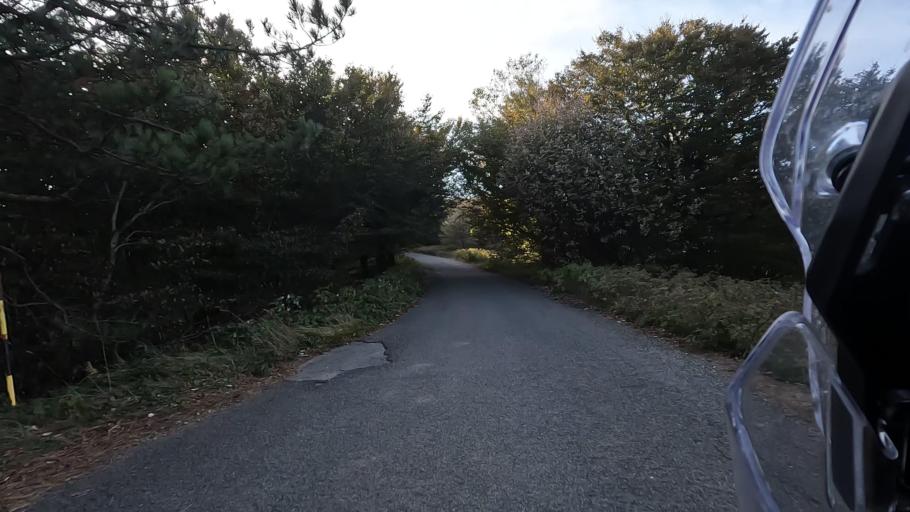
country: IT
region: Liguria
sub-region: Provincia di Genova
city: Sciarborasca
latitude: 44.4307
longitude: 8.5799
